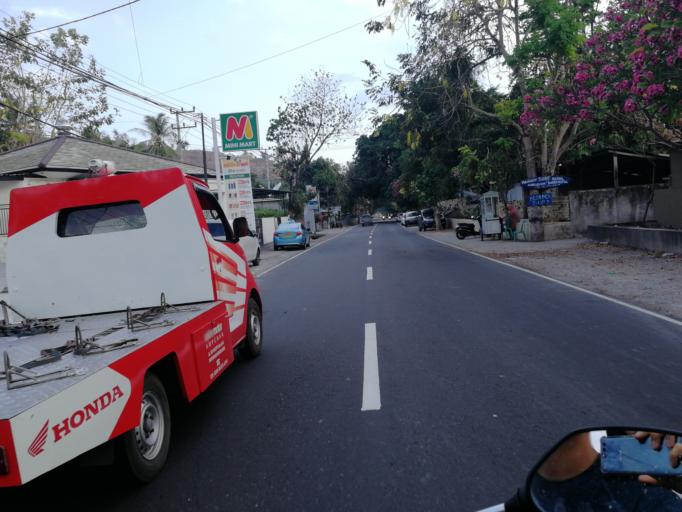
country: ID
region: West Nusa Tenggara
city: Karangsubagan
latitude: -8.4772
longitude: 116.0389
